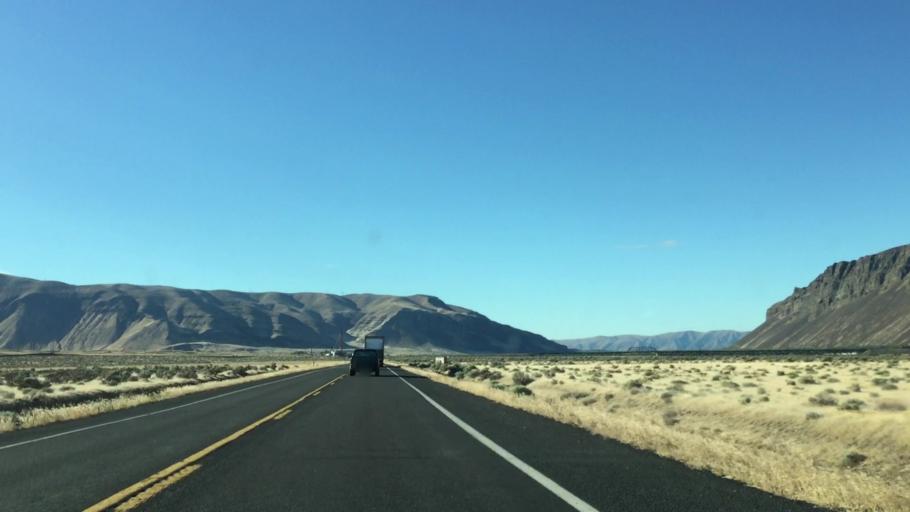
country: US
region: Washington
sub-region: Grant County
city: Mattawa
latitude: 46.8563
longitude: -119.9469
